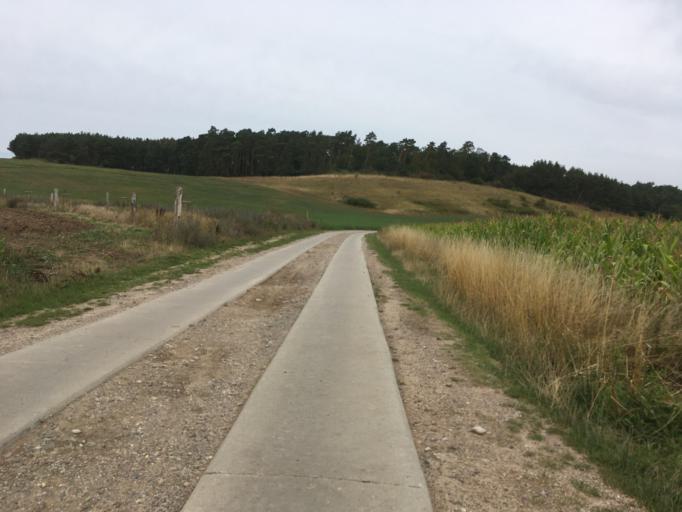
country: DE
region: Brandenburg
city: Gerswalde
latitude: 53.1869
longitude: 13.8338
